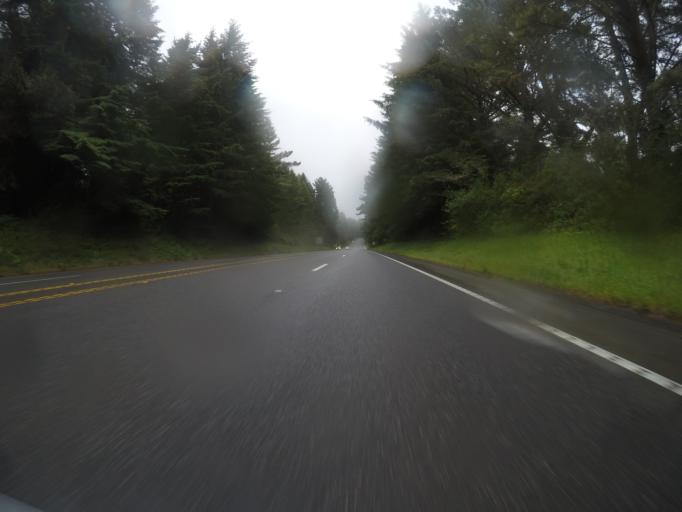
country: US
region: California
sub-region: Humboldt County
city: Westhaven-Moonstone
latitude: 41.0590
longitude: -124.1332
